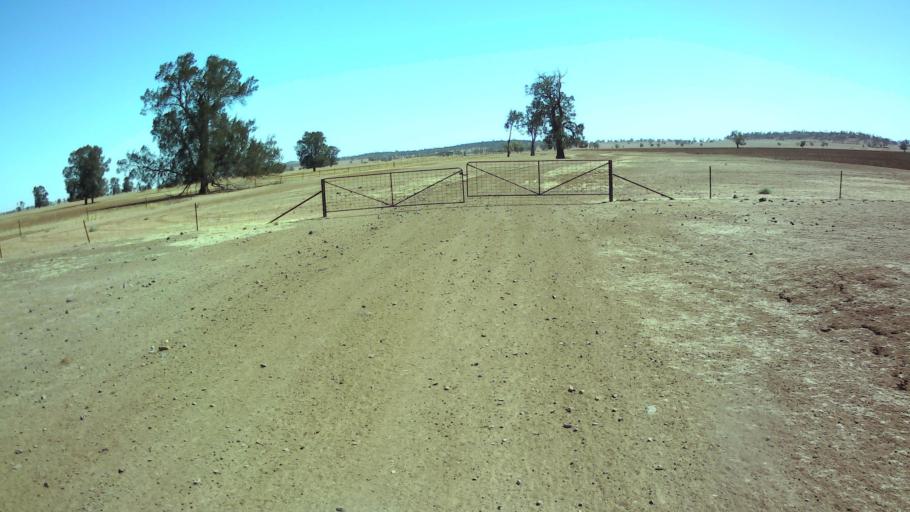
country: AU
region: New South Wales
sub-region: Forbes
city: Forbes
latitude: -33.7121
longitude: 147.6672
